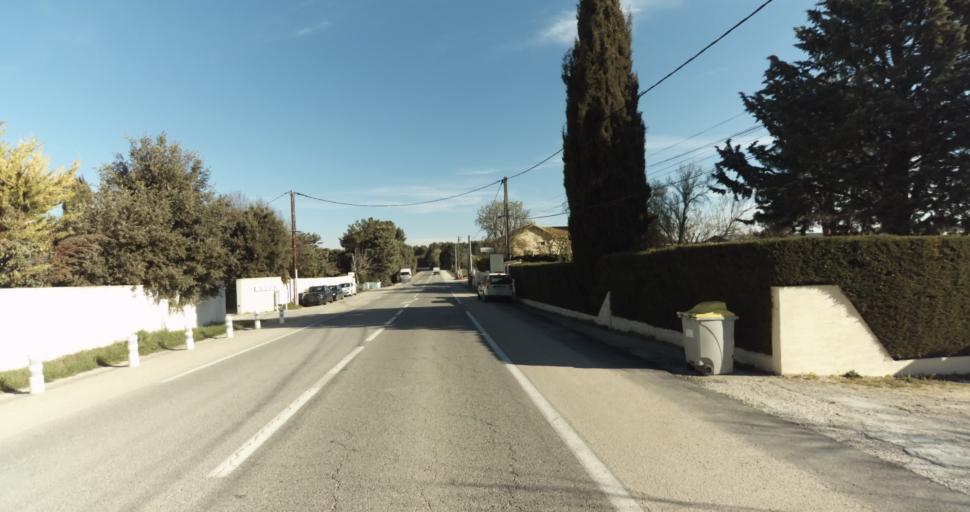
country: FR
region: Provence-Alpes-Cote d'Azur
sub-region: Departement des Bouches-du-Rhone
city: Aix-en-Provence
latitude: 43.5628
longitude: 5.4340
